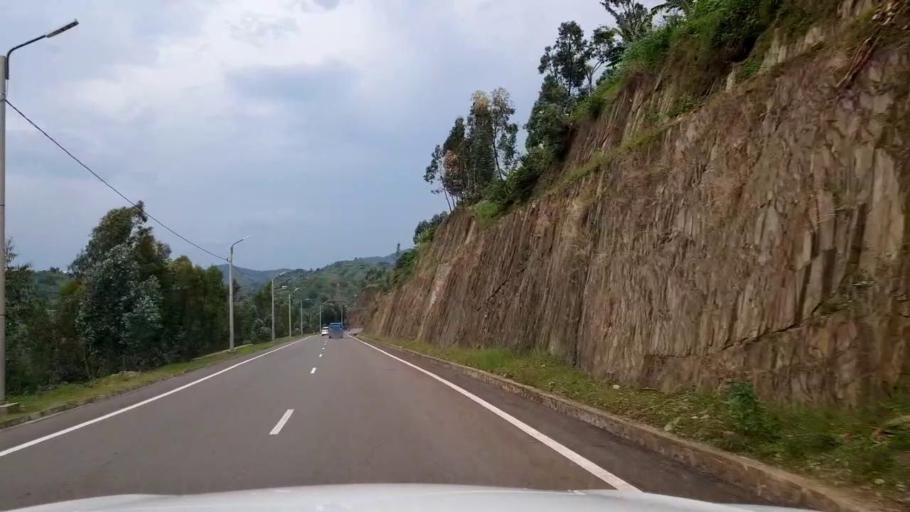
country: RW
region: Western Province
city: Kibuye
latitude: -2.0372
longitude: 29.4003
